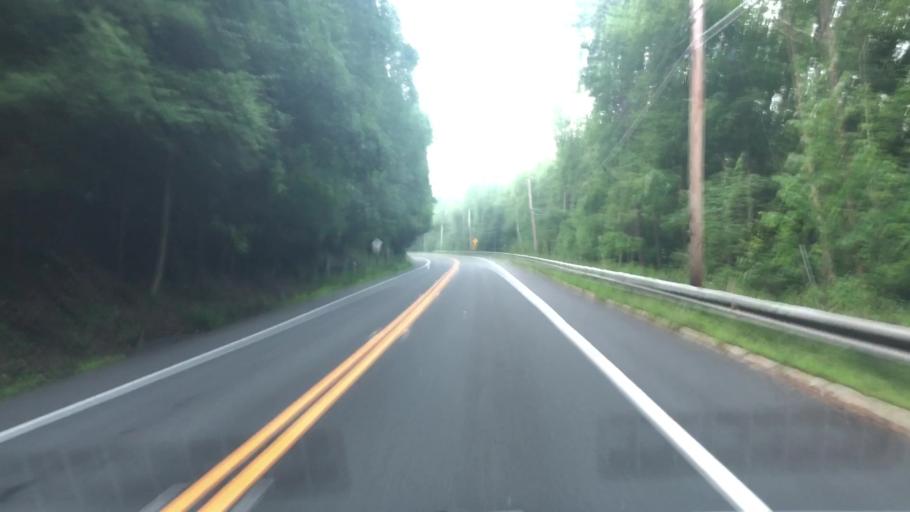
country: US
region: Massachusetts
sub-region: Franklin County
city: Ashfield
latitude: 42.5559
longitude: -72.8053
